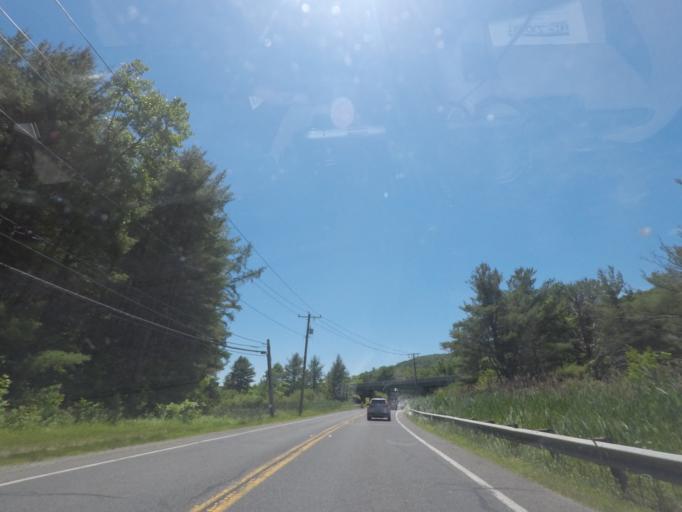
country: US
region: Massachusetts
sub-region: Berkshire County
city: Becket
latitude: 42.2783
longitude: -73.1415
